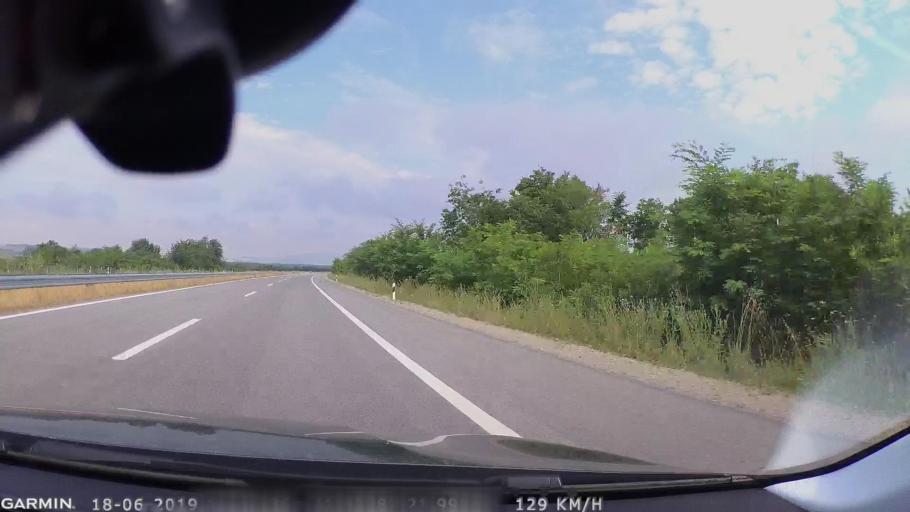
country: MK
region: Sveti Nikole
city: Sveti Nikole
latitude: 41.8302
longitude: 21.9972
